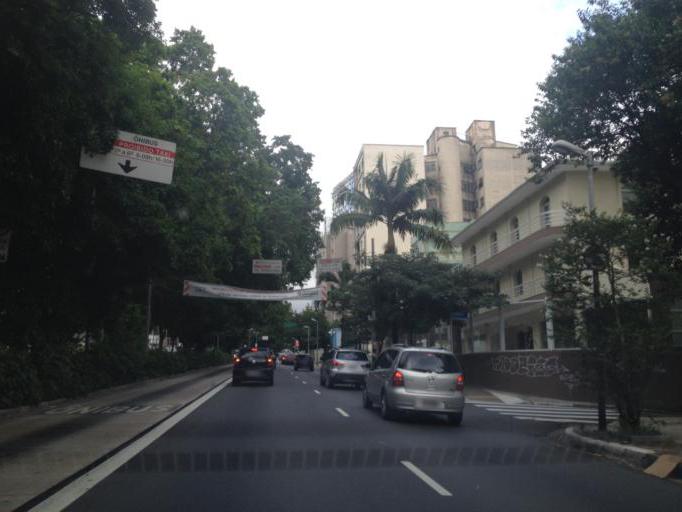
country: BR
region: Sao Paulo
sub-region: Sao Paulo
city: Sao Paulo
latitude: -23.5613
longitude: -46.6732
